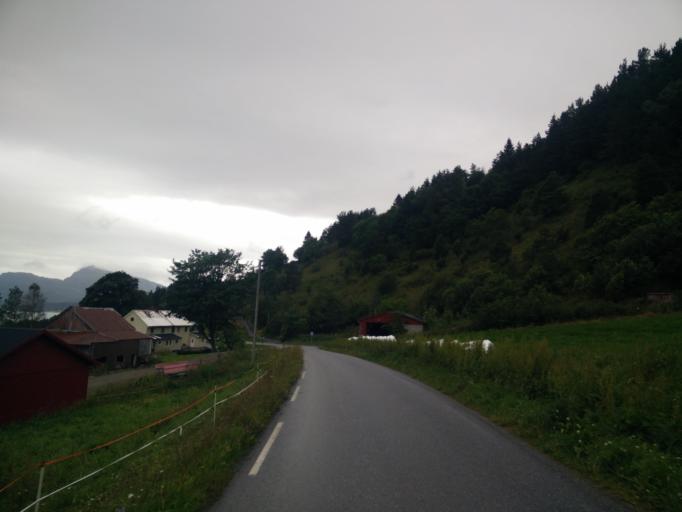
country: NO
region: More og Romsdal
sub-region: Kristiansund
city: Rensvik
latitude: 63.0153
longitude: 7.9110
